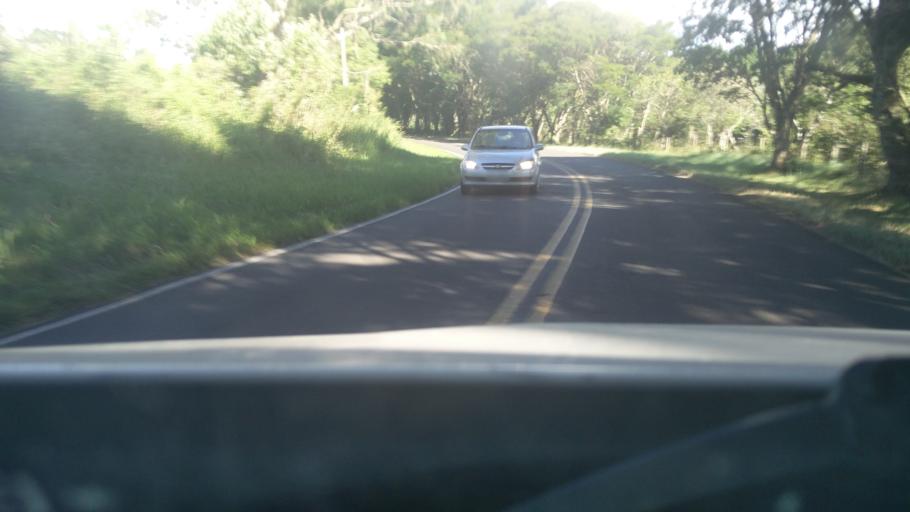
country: BR
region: Parana
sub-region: Palmeira
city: Palmeira
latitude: -25.4539
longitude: -49.8106
